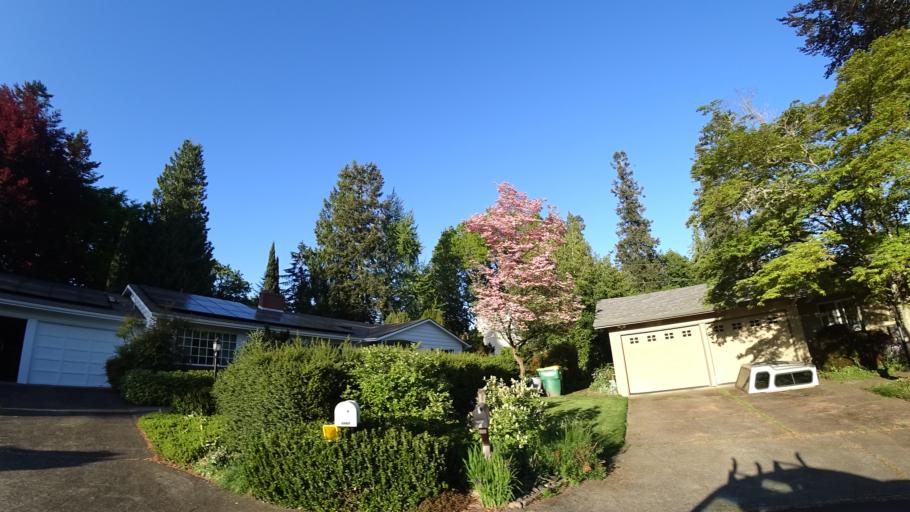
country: US
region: Oregon
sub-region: Washington County
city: West Slope
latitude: 45.4914
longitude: -122.7686
